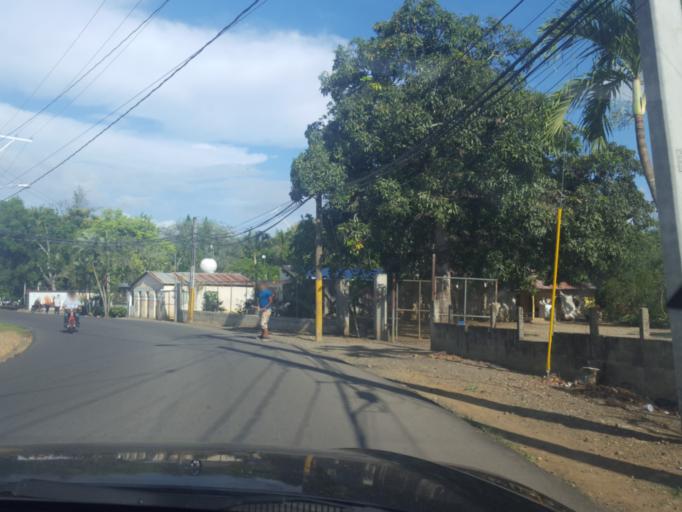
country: DO
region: La Vega
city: Rio Verde Arriba
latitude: 19.3444
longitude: -70.6204
